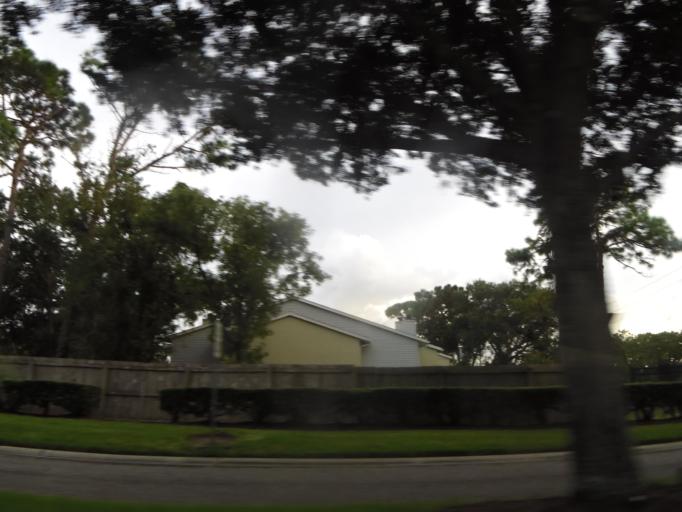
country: US
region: Florida
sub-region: Duval County
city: Atlantic Beach
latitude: 30.3670
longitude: -81.5024
